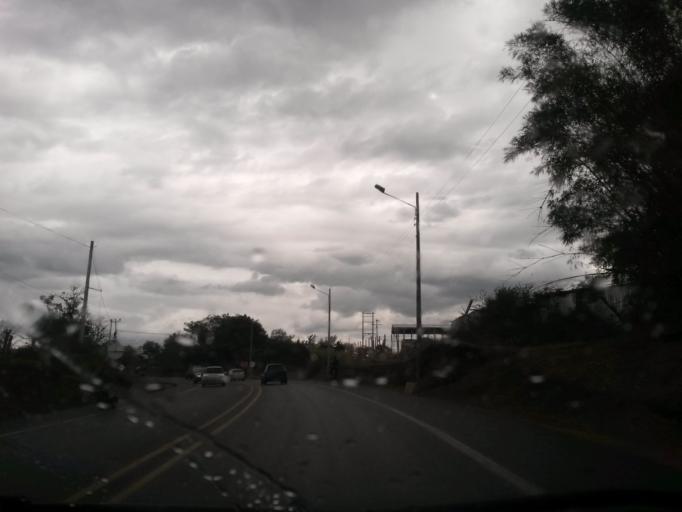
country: CO
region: Cauca
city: Popayan
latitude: 2.5002
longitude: -76.5574
